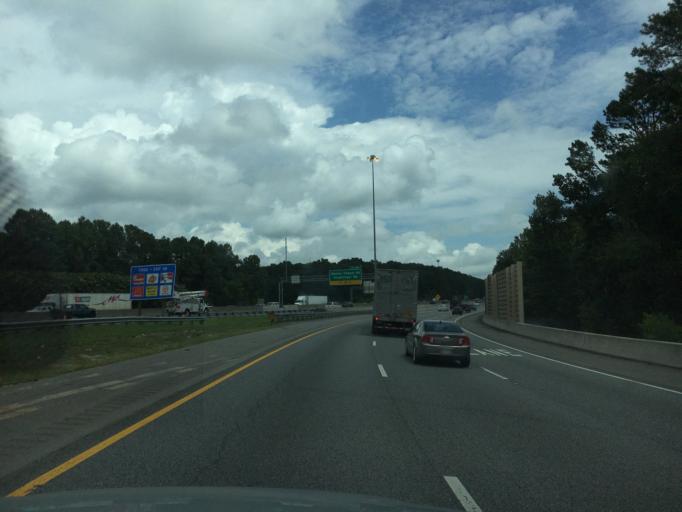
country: US
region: Georgia
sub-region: DeKalb County
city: Panthersville
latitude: 33.7138
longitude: -84.2389
